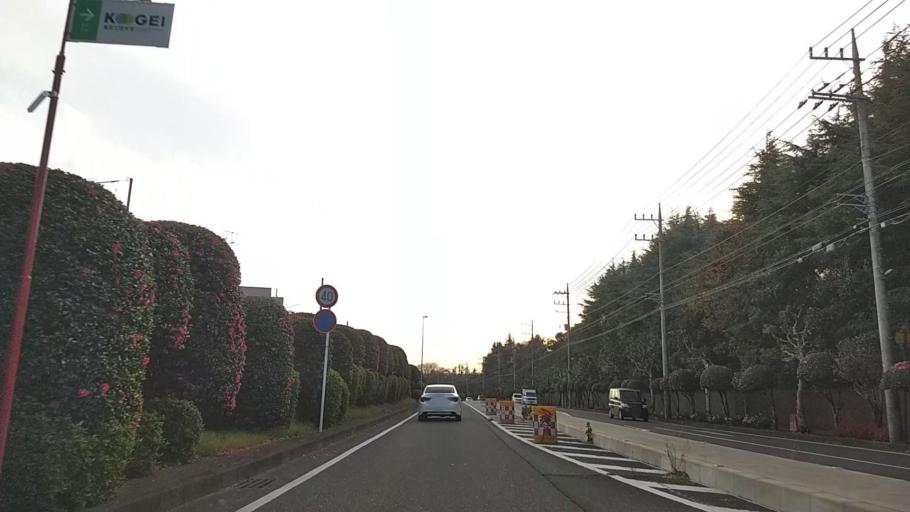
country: JP
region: Kanagawa
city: Atsugi
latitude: 35.4596
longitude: 139.3322
